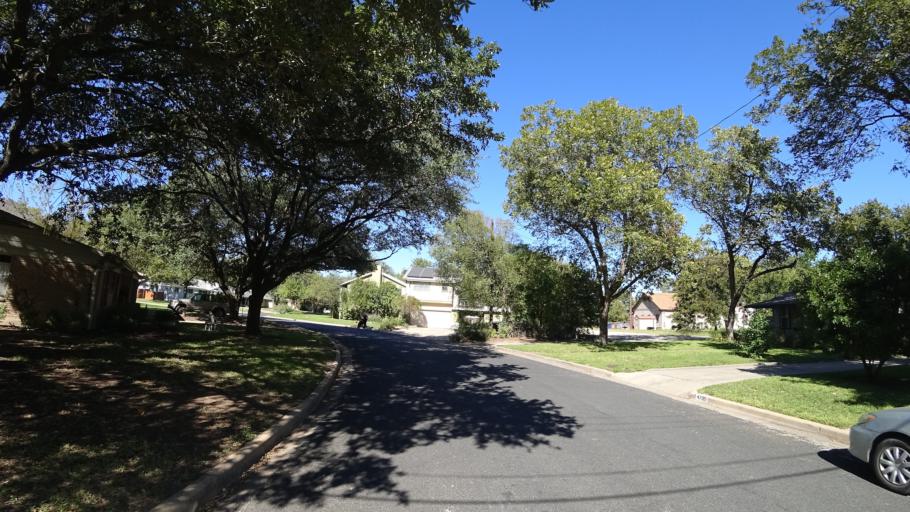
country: US
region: Texas
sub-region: Travis County
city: West Lake Hills
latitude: 30.3240
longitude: -97.7526
